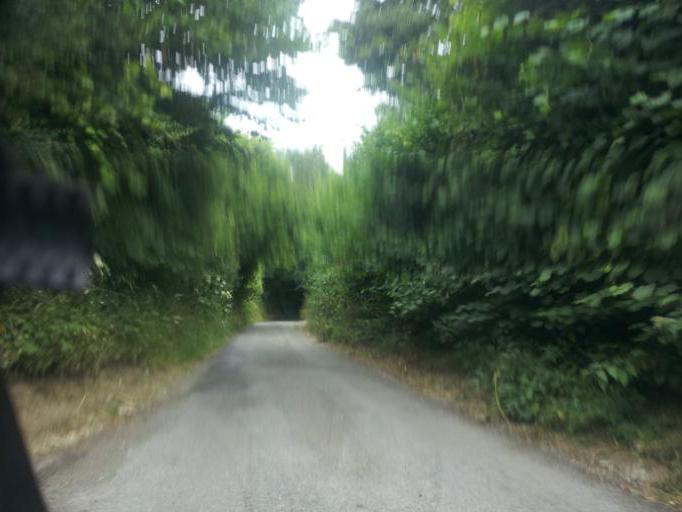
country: GB
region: England
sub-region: Kent
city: Meopham
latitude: 51.3601
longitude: 0.3779
